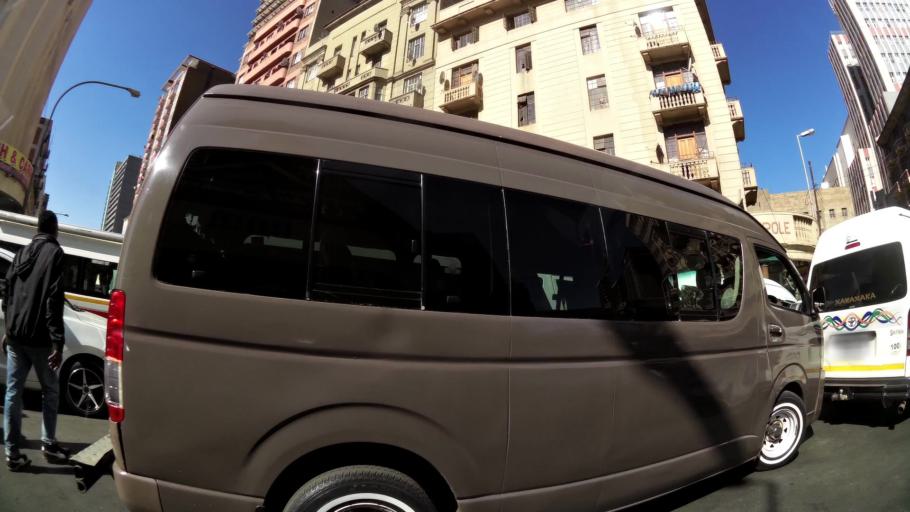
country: ZA
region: Gauteng
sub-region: City of Johannesburg Metropolitan Municipality
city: Johannesburg
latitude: -26.2004
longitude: 28.0454
